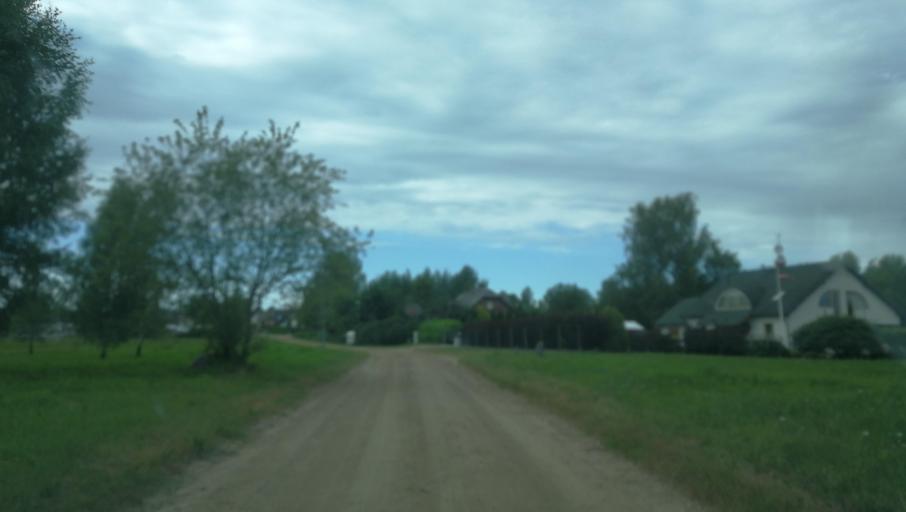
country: LV
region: Cesu Rajons
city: Cesis
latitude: 57.3014
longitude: 25.2881
